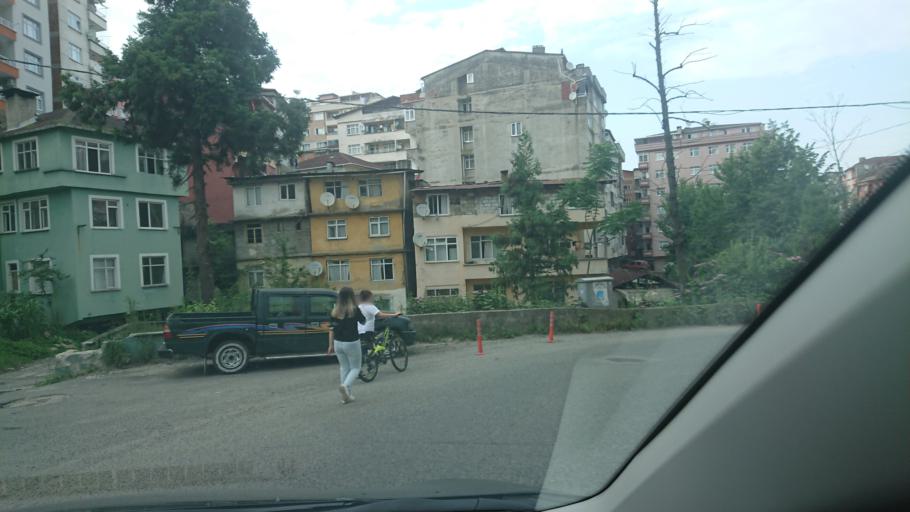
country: TR
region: Rize
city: Rize
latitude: 41.0198
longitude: 40.5168
